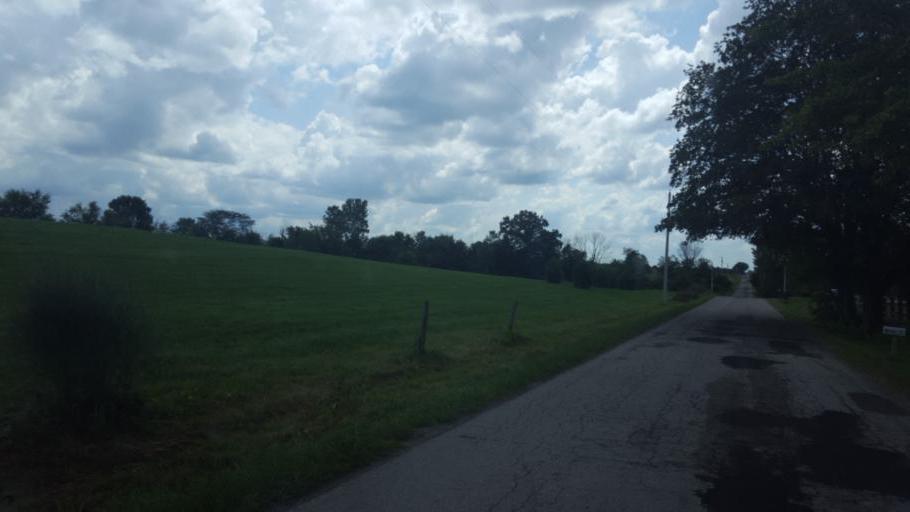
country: US
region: Ohio
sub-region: Knox County
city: Centerburg
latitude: 40.3808
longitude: -82.8003
